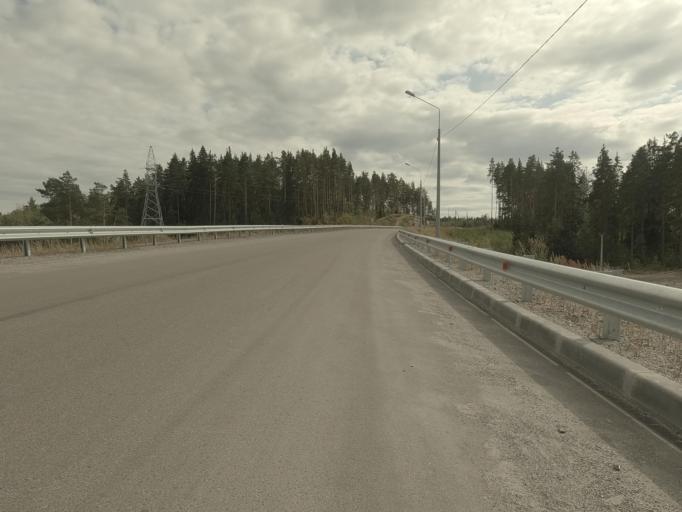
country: RU
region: Leningrad
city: Kamennogorsk
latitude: 60.9628
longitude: 29.1416
